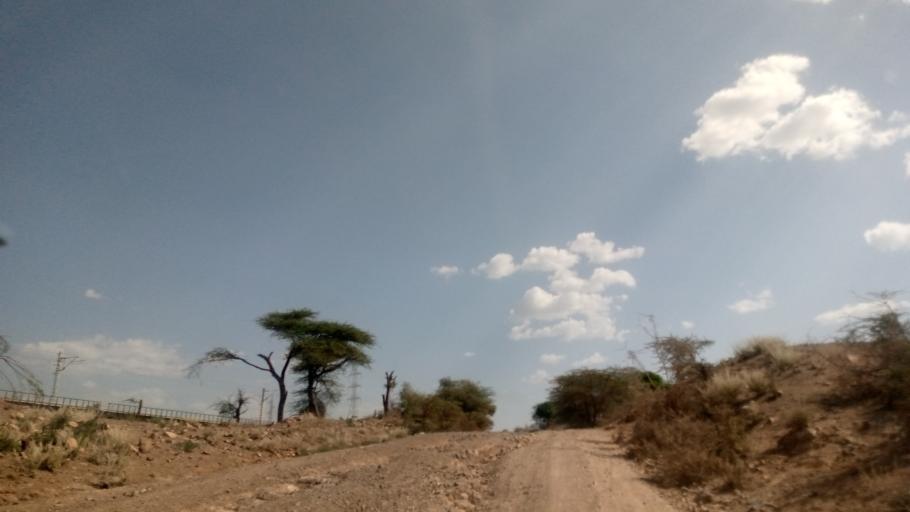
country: ET
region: Oromiya
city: Hirna
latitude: 9.5474
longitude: 41.1531
